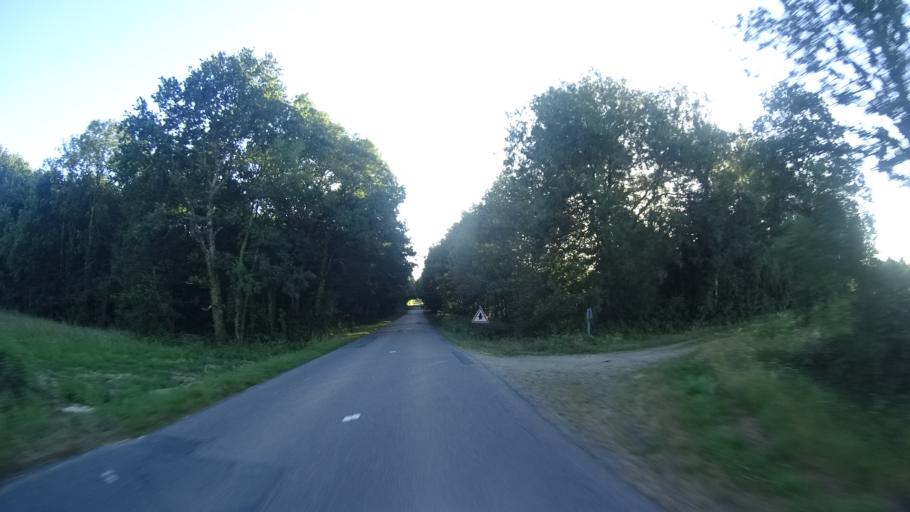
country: FR
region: Brittany
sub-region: Departement d'Ille-et-Vilaine
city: Saint-Just
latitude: 47.7190
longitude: -1.9188
